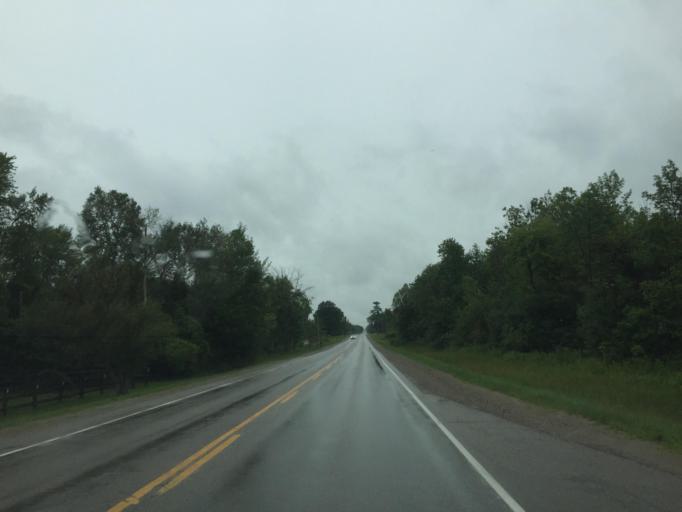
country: CA
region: Ontario
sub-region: Wellington County
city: Guelph
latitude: 43.4463
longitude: -80.2457
